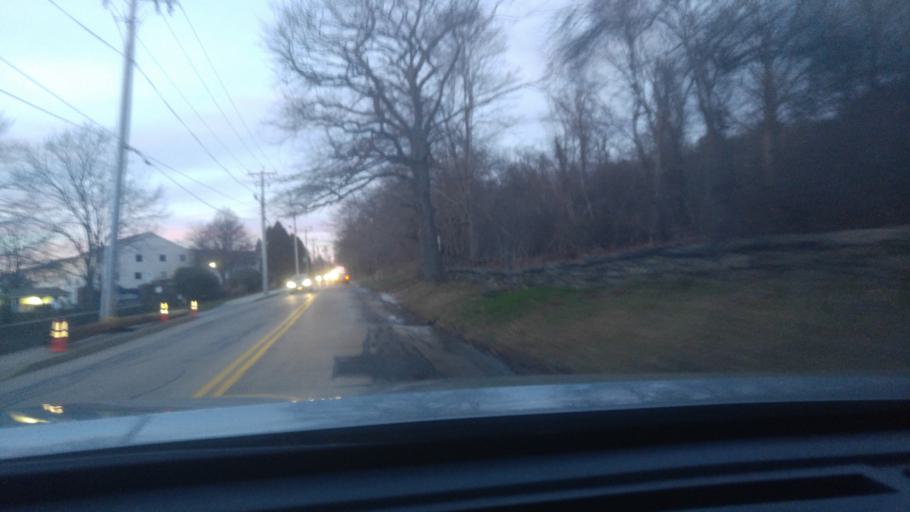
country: US
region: Rhode Island
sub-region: Newport County
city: Newport
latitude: 41.5095
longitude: -71.3125
